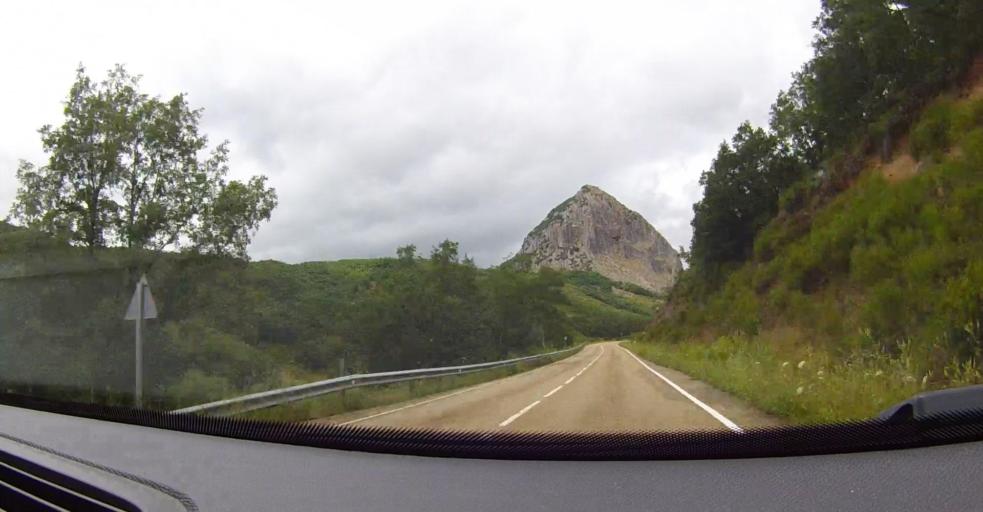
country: ES
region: Castille and Leon
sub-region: Provincia de Leon
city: Reyero
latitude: 42.9503
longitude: -5.2457
